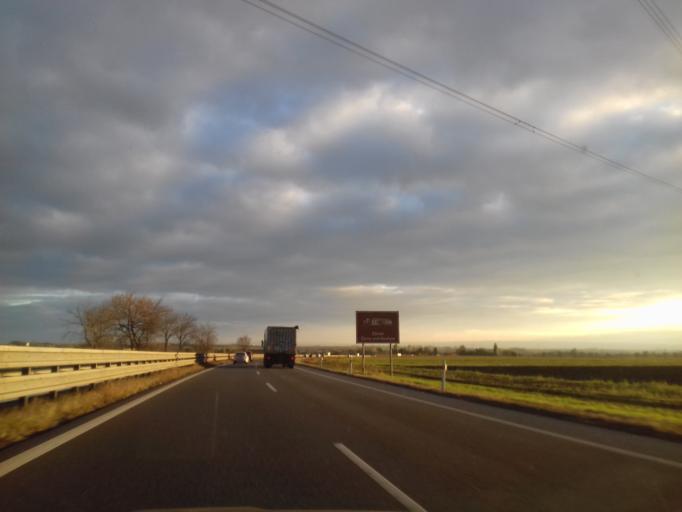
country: CZ
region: Olomoucky
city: Lutin
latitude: 49.5248
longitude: 17.1551
